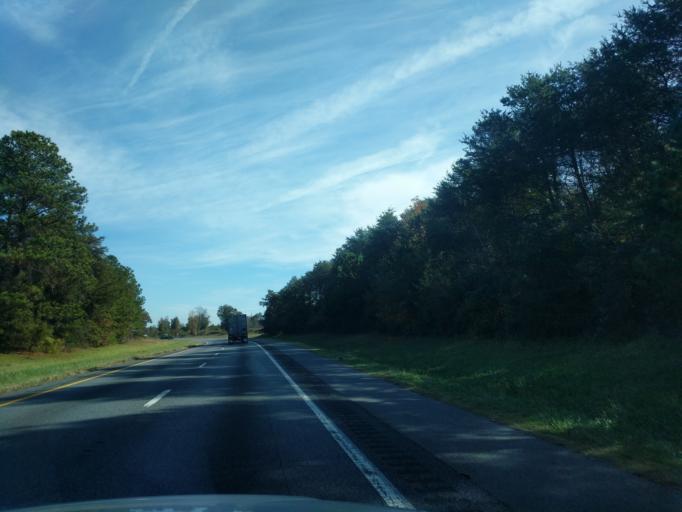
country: US
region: South Carolina
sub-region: Cherokee County
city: East Gaffney
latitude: 35.1026
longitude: -81.6251
